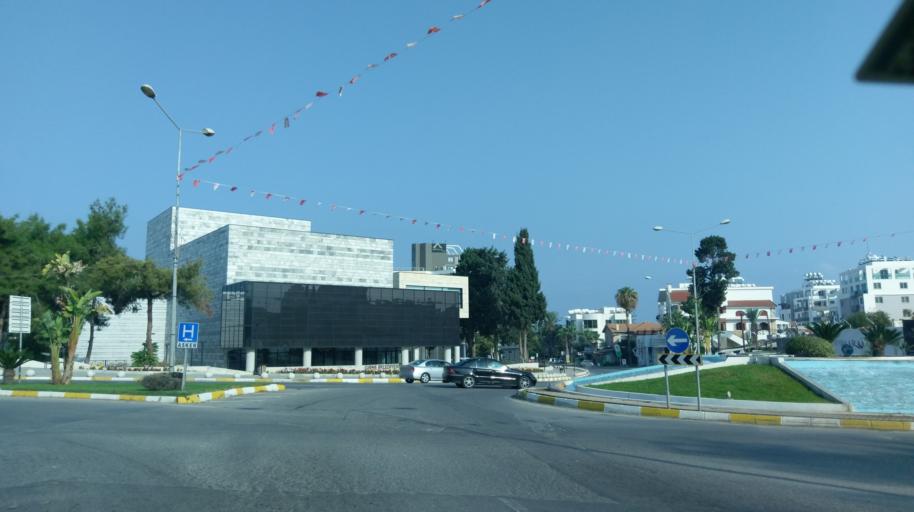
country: CY
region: Keryneia
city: Kyrenia
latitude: 35.3321
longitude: 33.3195
